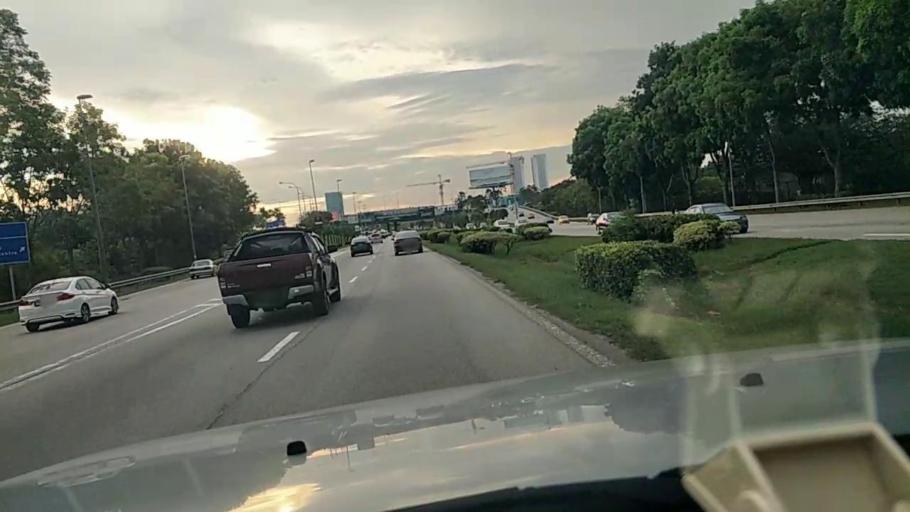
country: MY
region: Selangor
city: Shah Alam
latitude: 3.1031
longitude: 101.4726
